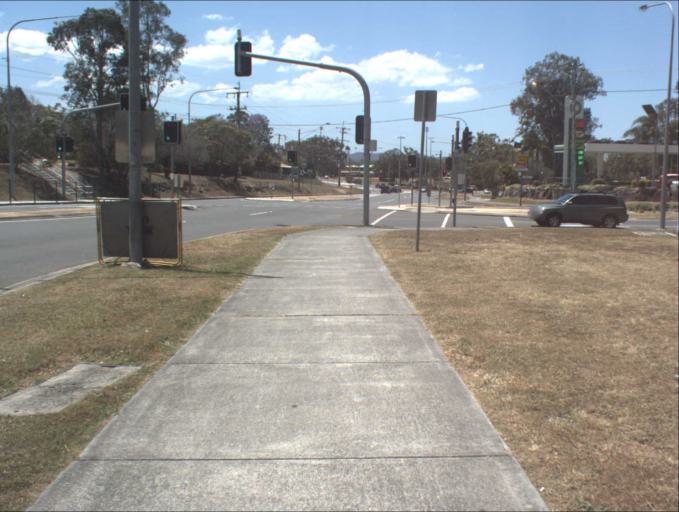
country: AU
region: Queensland
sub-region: Logan
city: Windaroo
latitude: -27.7236
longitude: 153.1944
